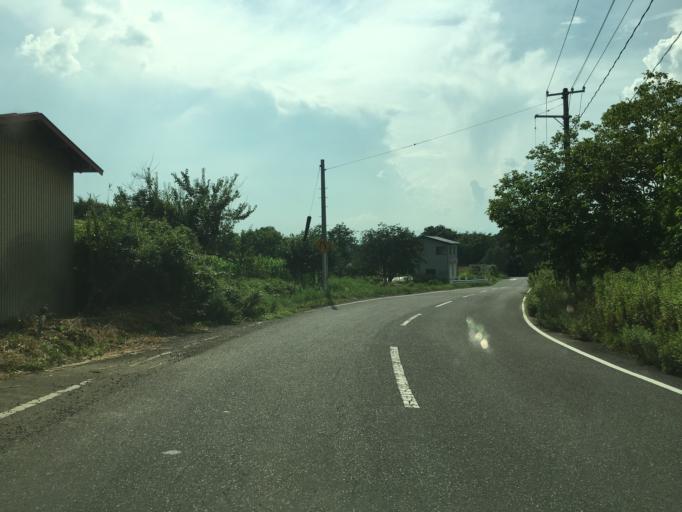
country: JP
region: Fukushima
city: Sukagawa
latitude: 37.3302
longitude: 140.4221
